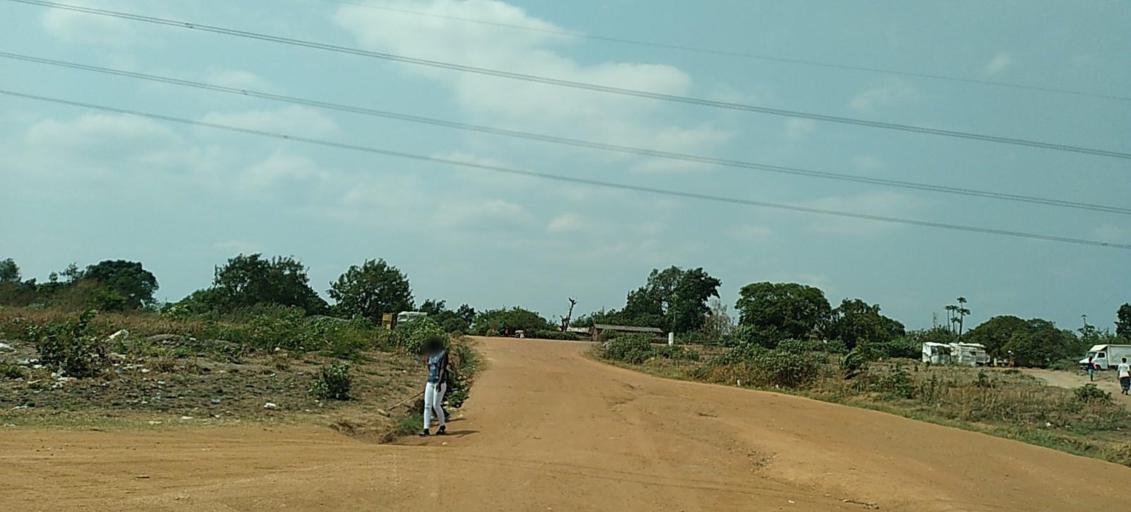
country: ZM
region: Copperbelt
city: Chambishi
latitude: -12.6343
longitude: 28.0694
